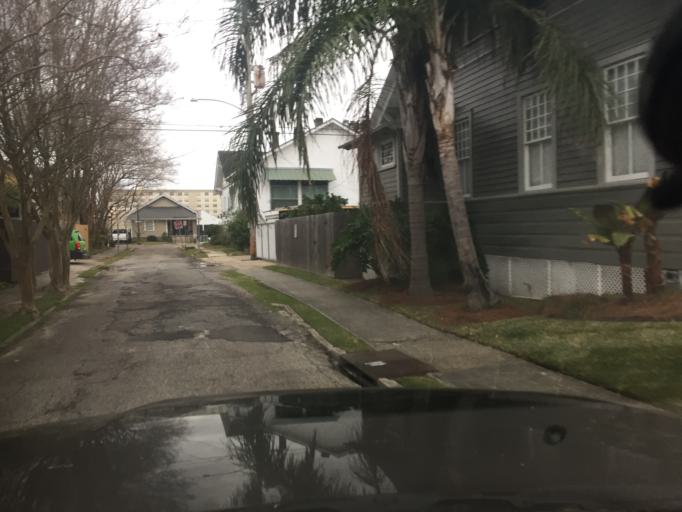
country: US
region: Louisiana
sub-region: Orleans Parish
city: New Orleans
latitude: 29.9829
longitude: -90.0856
